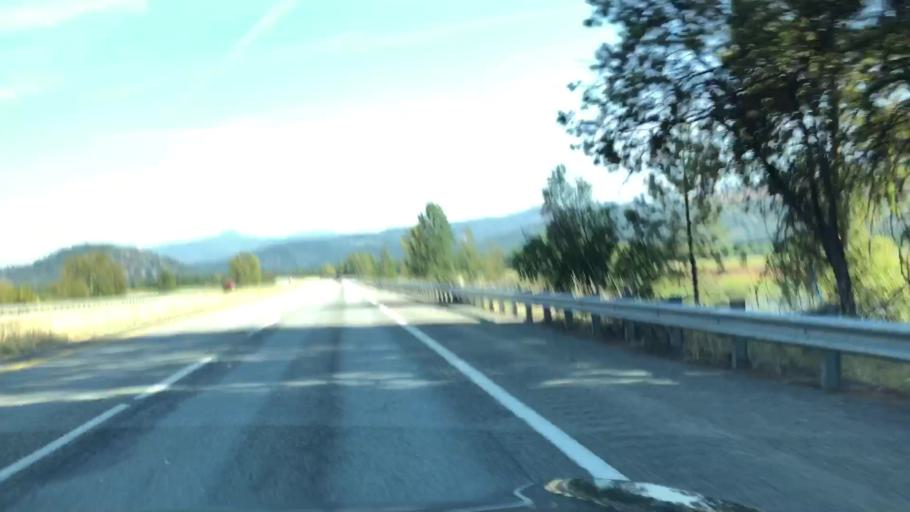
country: US
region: Idaho
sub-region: Shoshone County
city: Pinehurst
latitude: 47.5610
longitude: -116.3968
